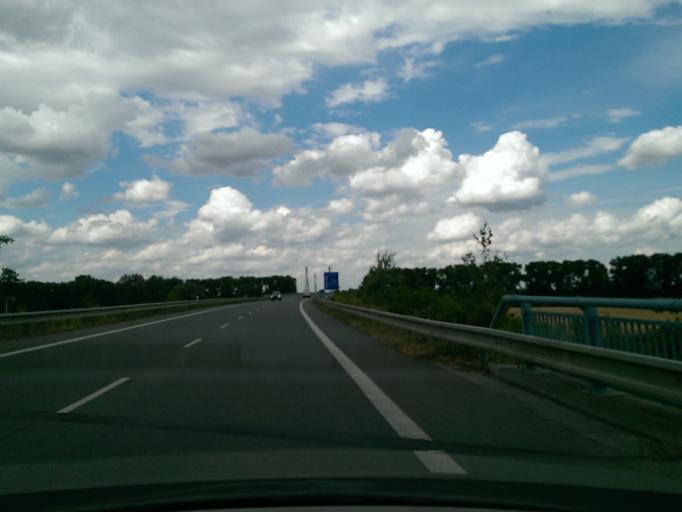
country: CZ
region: Central Bohemia
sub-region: Okres Nymburk
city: Podebrady
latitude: 50.1618
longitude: 15.0875
